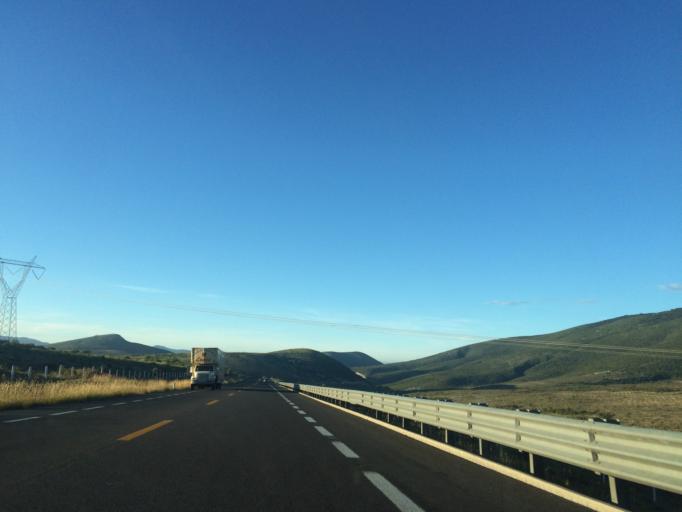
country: MX
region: Puebla
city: Morelos Canada
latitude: 18.6951
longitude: -97.4637
